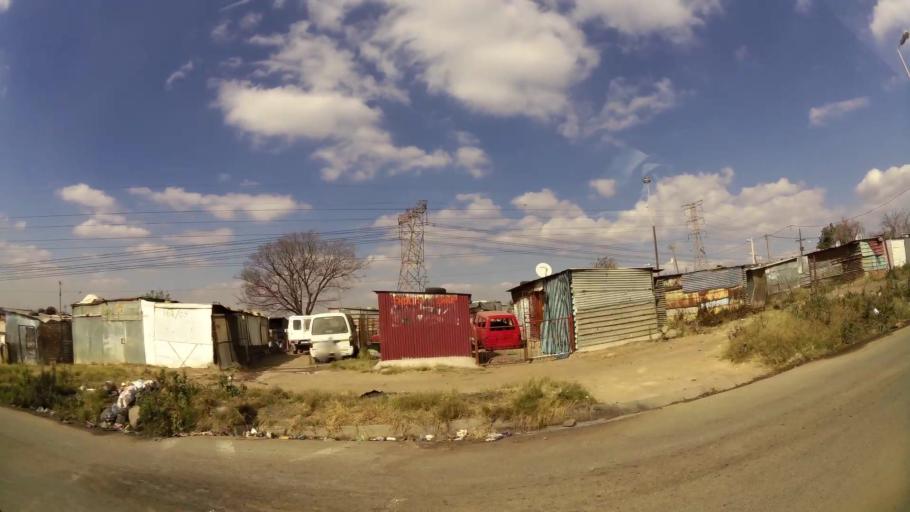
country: ZA
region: Gauteng
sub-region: Ekurhuleni Metropolitan Municipality
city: Tembisa
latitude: -26.0045
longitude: 28.1858
